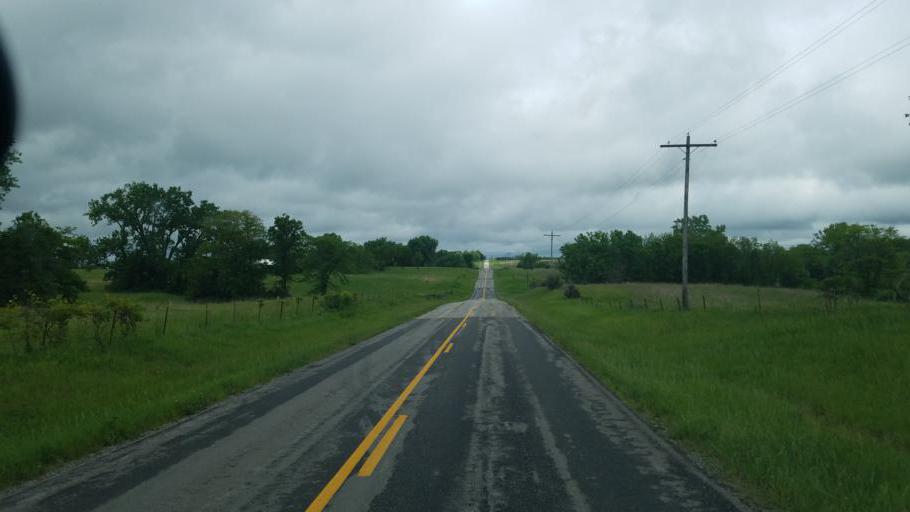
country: US
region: Missouri
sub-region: Mercer County
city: Princeton
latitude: 40.4098
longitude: -93.6848
